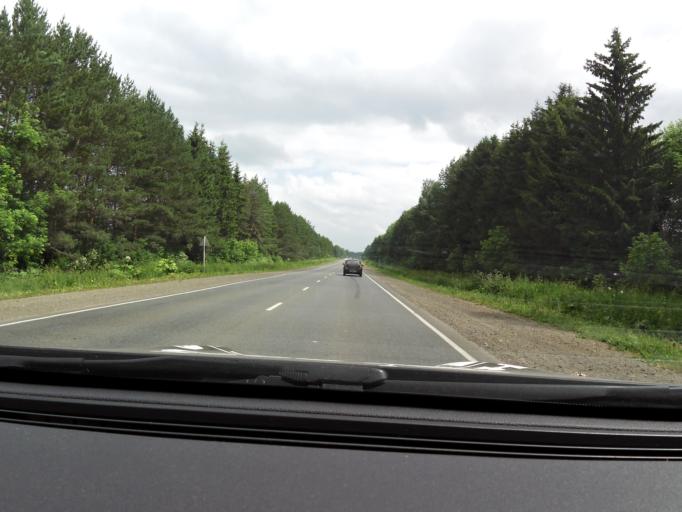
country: RU
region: Perm
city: Kungur
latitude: 57.4520
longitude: 56.7868
